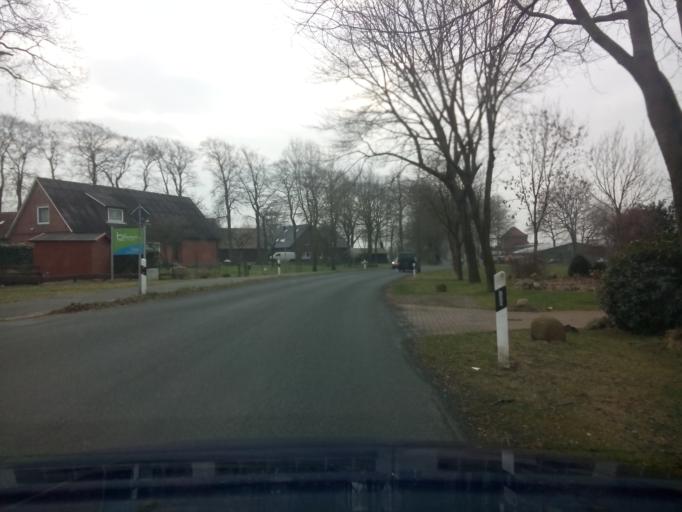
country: DE
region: Lower Saxony
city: Kuhrstedt
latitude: 53.6148
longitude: 8.8286
